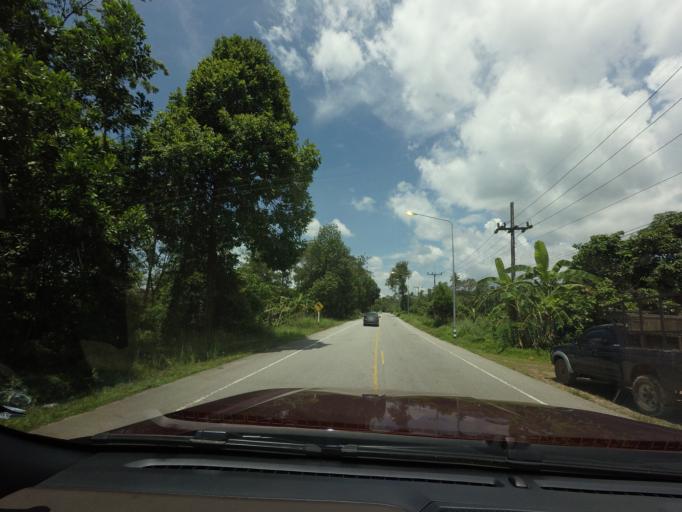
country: TH
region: Narathiwat
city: Chanae
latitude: 6.2002
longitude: 101.6871
